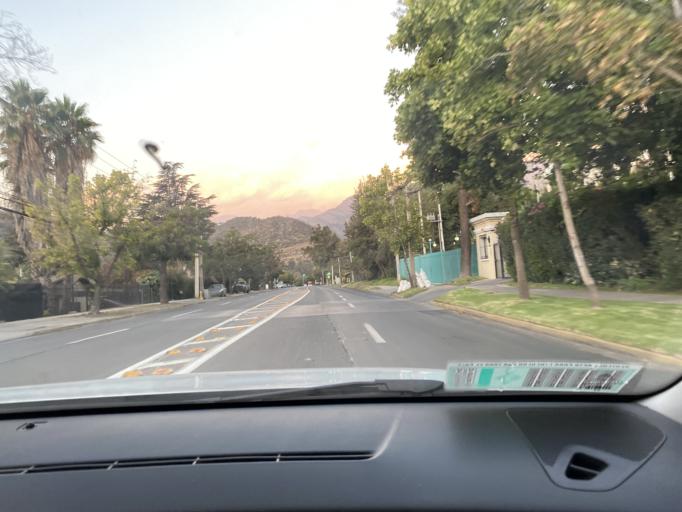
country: CL
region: Santiago Metropolitan
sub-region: Provincia de Santiago
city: Villa Presidente Frei, Nunoa, Santiago, Chile
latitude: -33.3662
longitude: -70.4978
